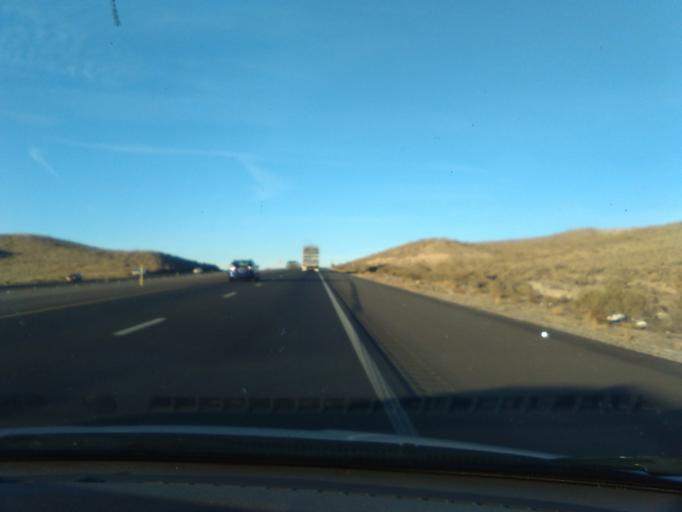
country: US
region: New Mexico
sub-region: Bernalillo County
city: South Valley
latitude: 34.9825
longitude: -106.6512
